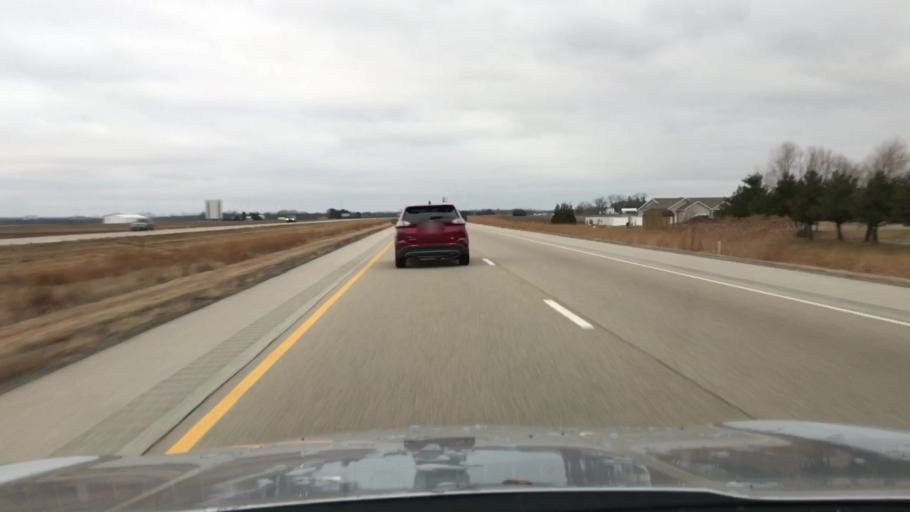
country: US
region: Illinois
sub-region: Logan County
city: Lincoln
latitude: 40.1833
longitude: -89.3373
